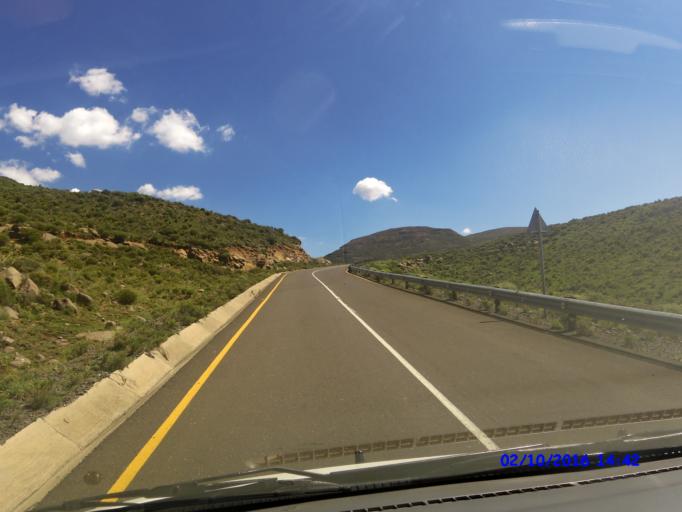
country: LS
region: Maseru
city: Nako
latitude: -29.5280
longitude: 28.0601
